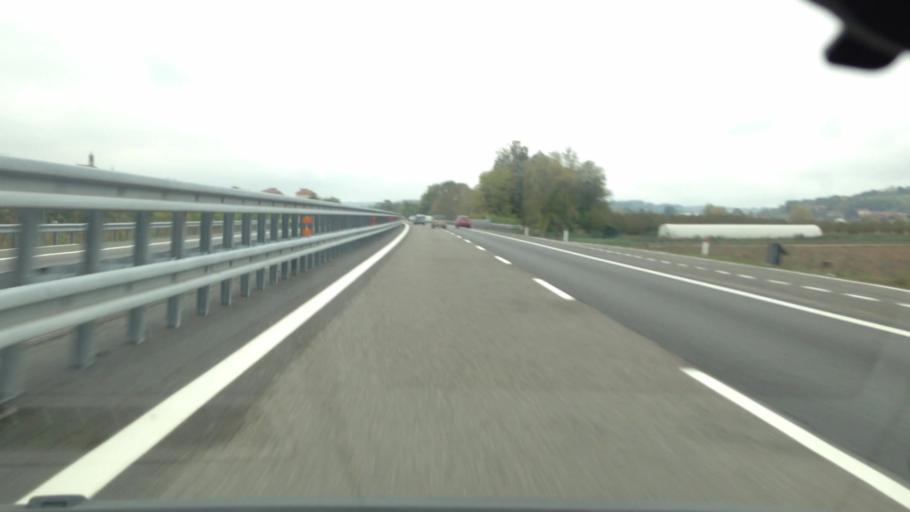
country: IT
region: Piedmont
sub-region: Provincia di Asti
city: Villafranca d'Asti
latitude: 44.9104
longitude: 8.0468
